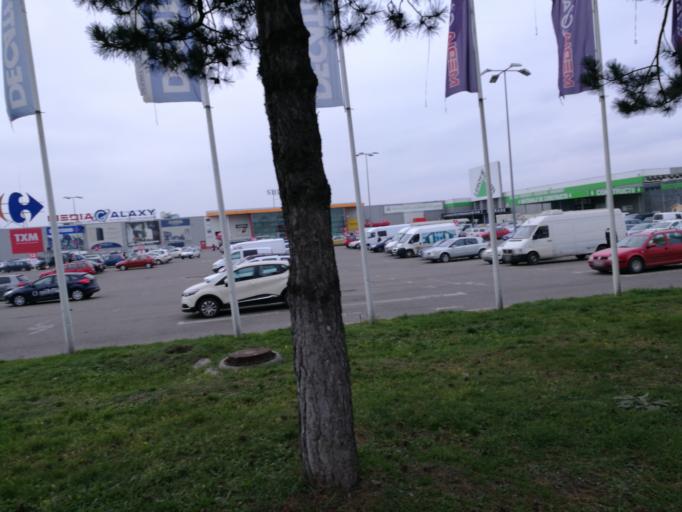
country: RO
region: Suceava
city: Suceava
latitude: 47.6645
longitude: 26.2692
